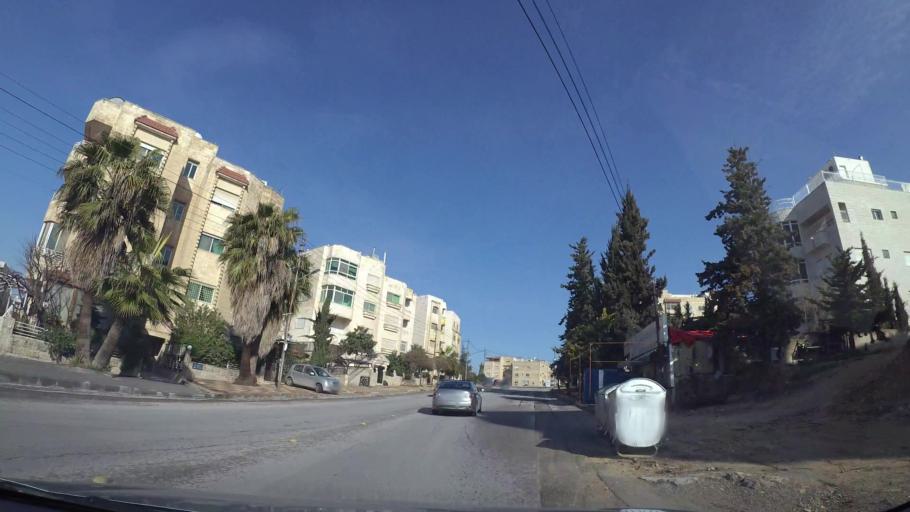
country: JO
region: Amman
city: Al Jubayhah
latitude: 32.0049
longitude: 35.8514
